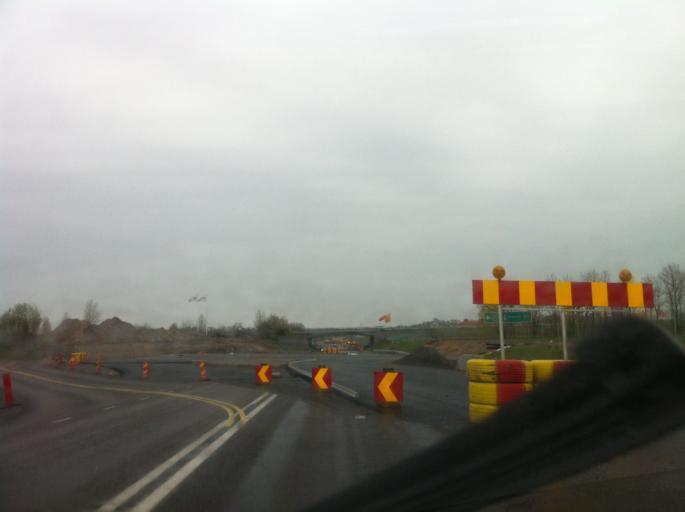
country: SE
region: Halland
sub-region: Falkenbergs Kommun
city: Falkenberg
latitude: 56.9297
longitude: 12.5138
